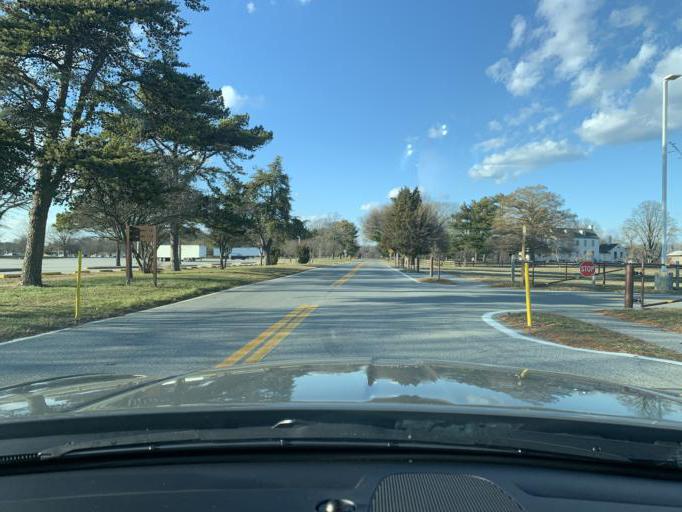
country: US
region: Maryland
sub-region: Anne Arundel County
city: Cape Saint Claire
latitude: 39.0130
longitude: -76.3987
